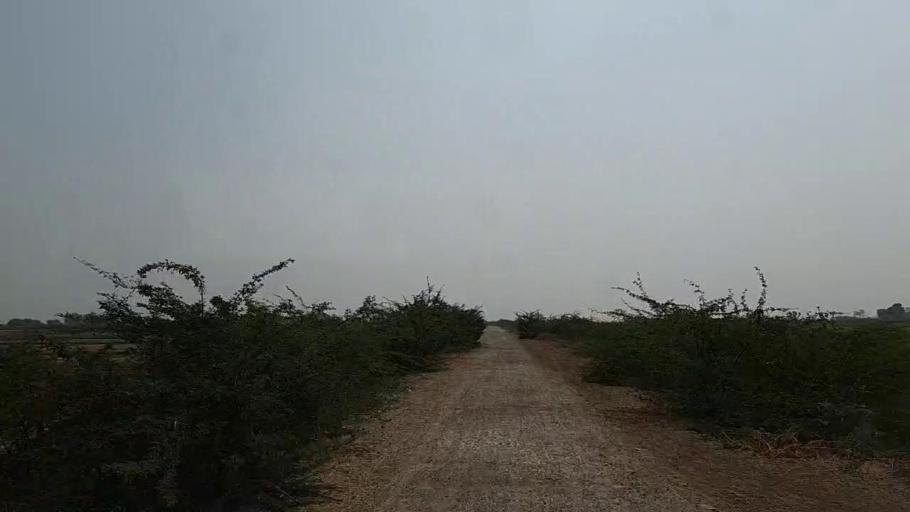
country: PK
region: Sindh
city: Naukot
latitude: 24.7867
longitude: 69.3295
